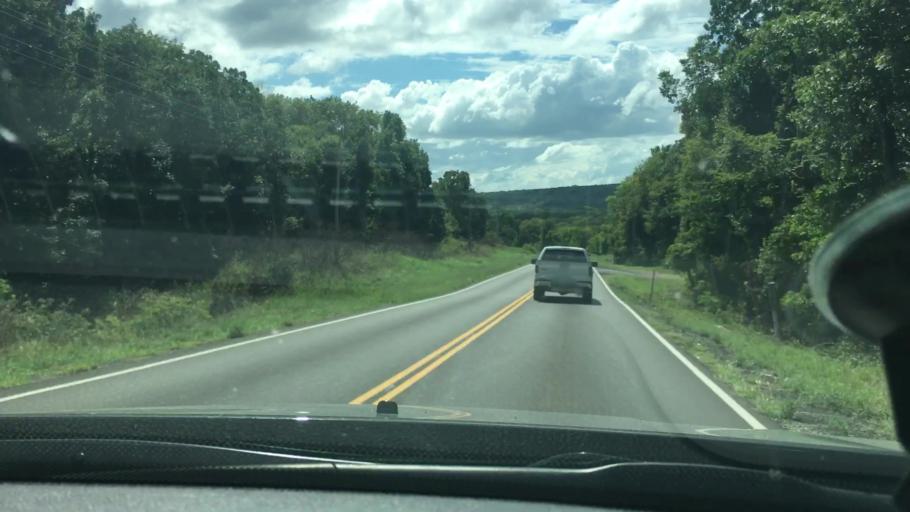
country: US
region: Oklahoma
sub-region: Sequoyah County
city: Vian
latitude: 35.6483
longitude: -94.9563
